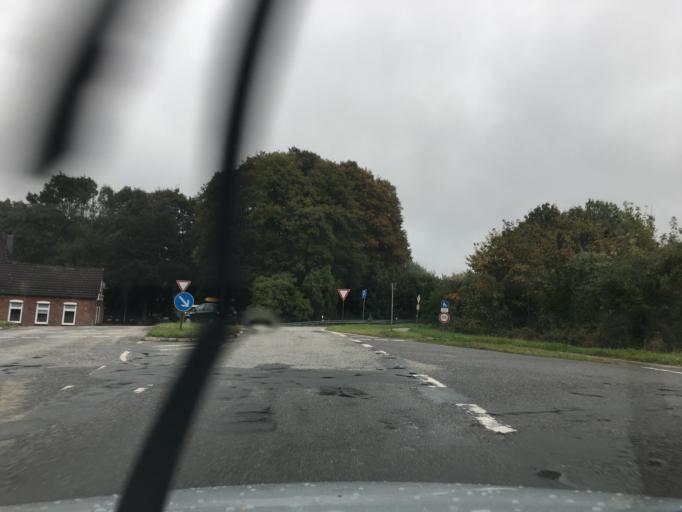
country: DE
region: Schleswig-Holstein
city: Ottendorf
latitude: 54.3688
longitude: 10.0617
